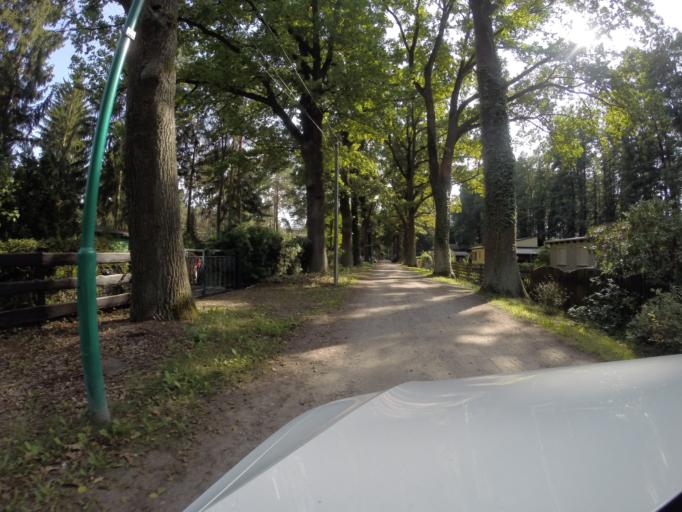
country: DE
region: Brandenburg
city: Baruth
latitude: 52.1211
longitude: 13.5280
